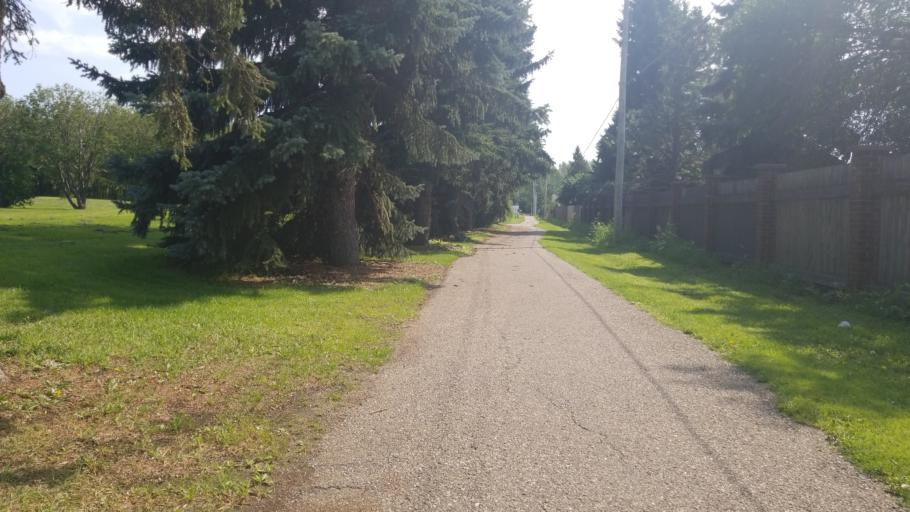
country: CA
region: Saskatchewan
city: Lloydminster
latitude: 53.2726
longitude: -110.0177
